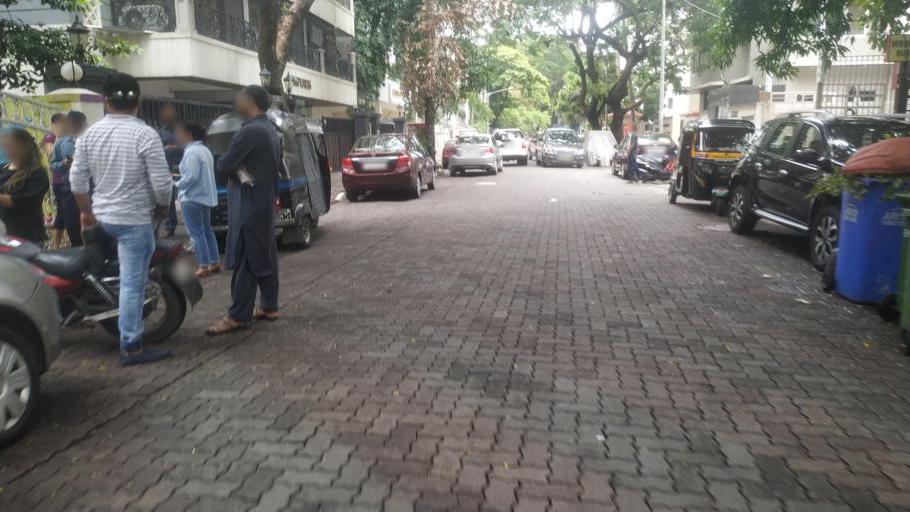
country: IN
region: Maharashtra
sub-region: Mumbai Suburban
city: Mumbai
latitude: 19.0588
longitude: 72.8325
